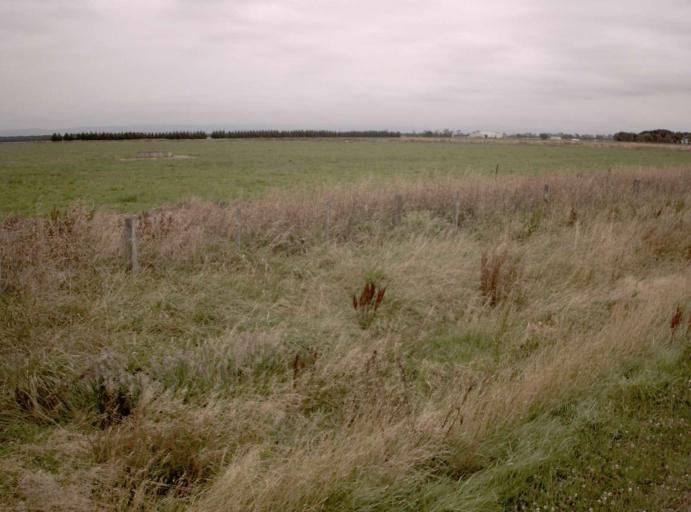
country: AU
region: Victoria
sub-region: Wellington
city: Heyfield
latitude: -38.0856
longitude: 146.7718
